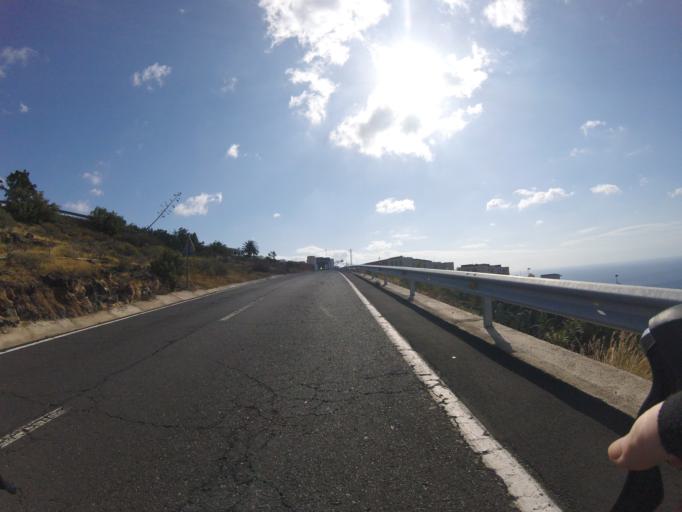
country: ES
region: Canary Islands
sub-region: Provincia de Santa Cruz de Tenerife
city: La Laguna
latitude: 28.4130
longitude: -16.3241
